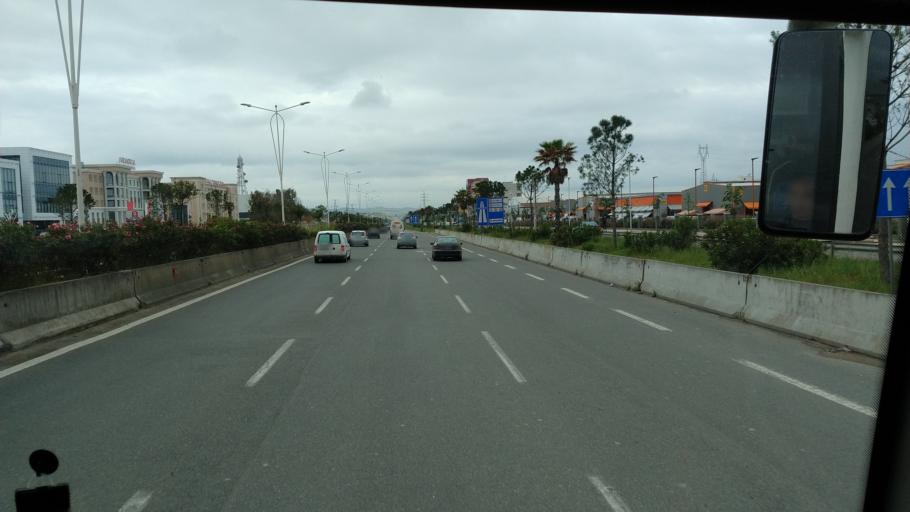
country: AL
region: Tirane
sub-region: Rrethi i Tiranes
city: Paskuqan
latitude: 41.3451
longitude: 19.7700
